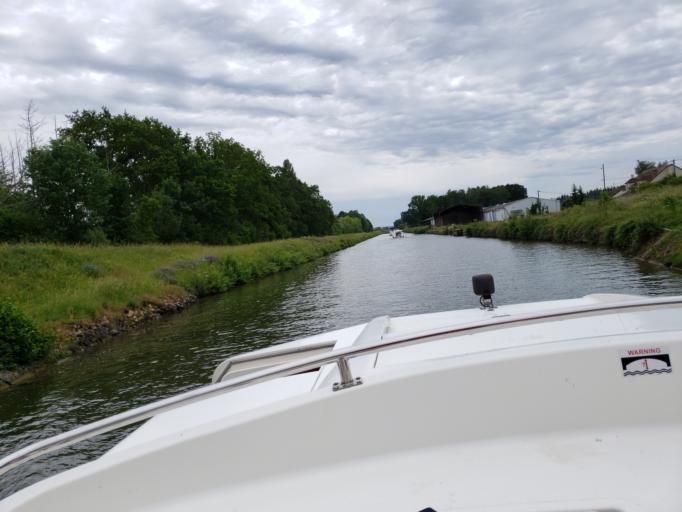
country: FR
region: Bourgogne
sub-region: Departement de l'Yonne
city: Appoigny
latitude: 47.8866
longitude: 3.5439
